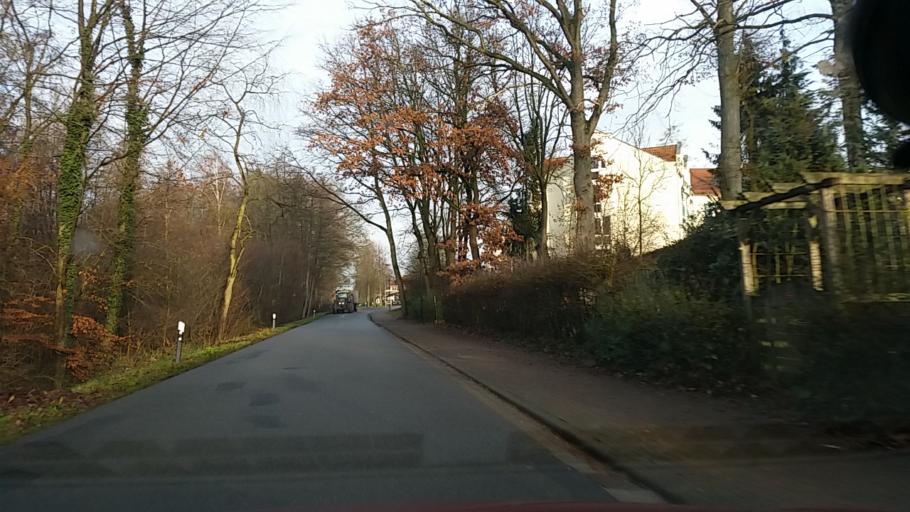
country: DE
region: Lower Saxony
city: Bodenteich
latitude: 52.8259
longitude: 10.6824
